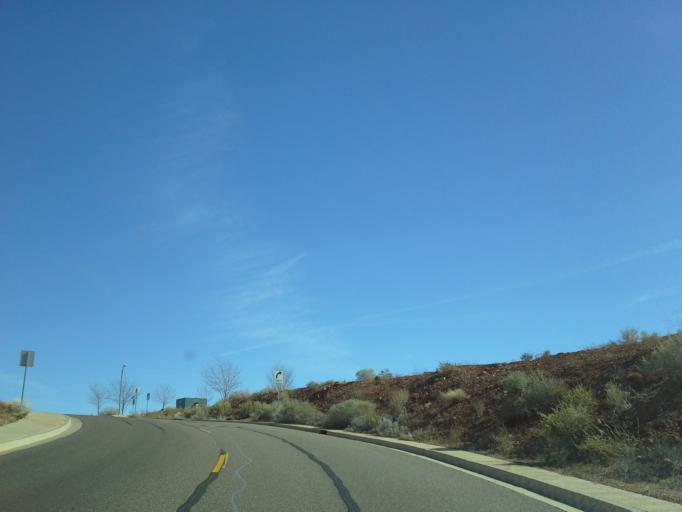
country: US
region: Arizona
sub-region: Coconino County
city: Page
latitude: 36.9358
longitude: -111.4652
